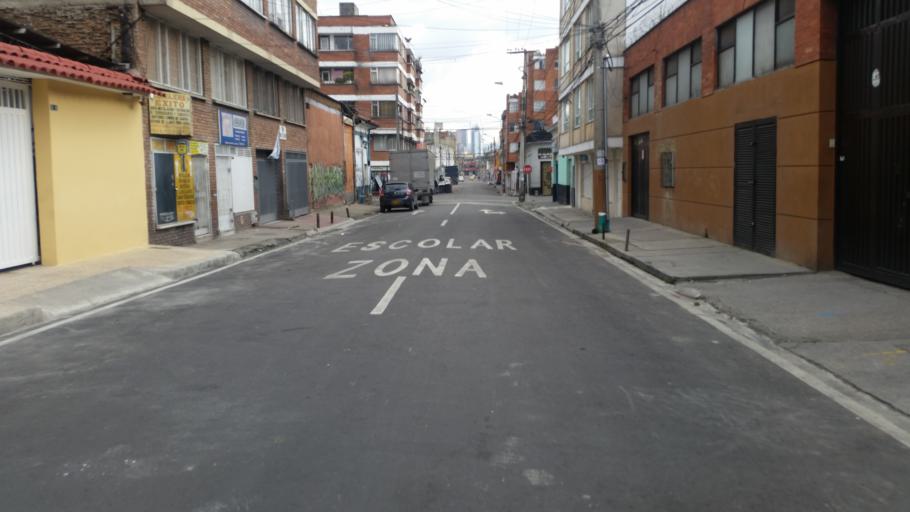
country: CO
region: Bogota D.C.
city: Bogota
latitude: 4.6478
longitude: -74.0659
